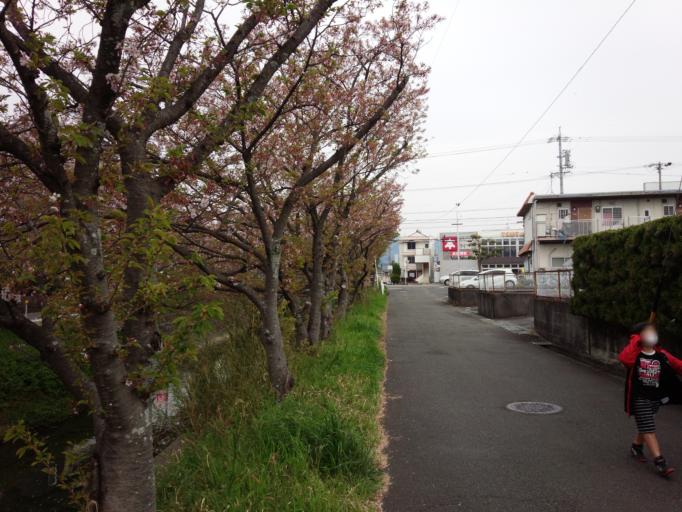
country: JP
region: Shizuoka
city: Shizuoka-shi
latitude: 35.0105
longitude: 138.4711
